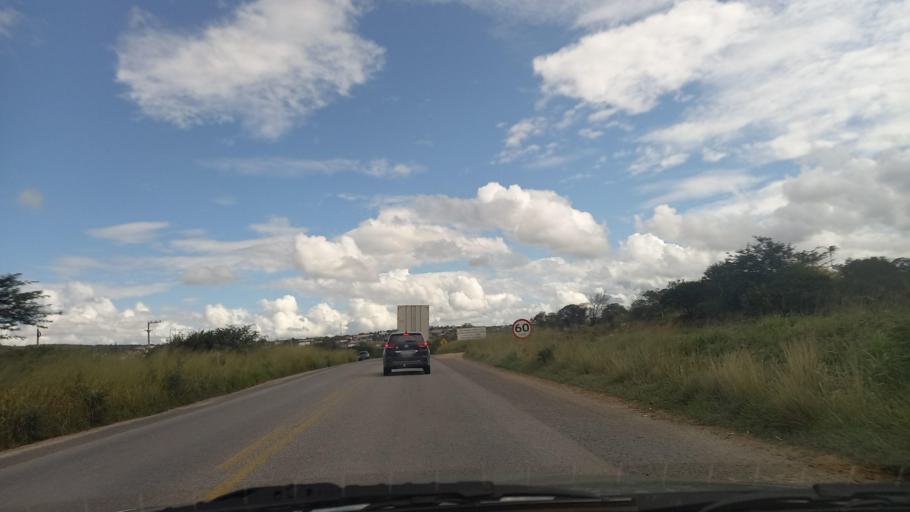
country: BR
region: Pernambuco
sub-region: Lajedo
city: Lajedo
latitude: -8.6946
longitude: -36.4129
